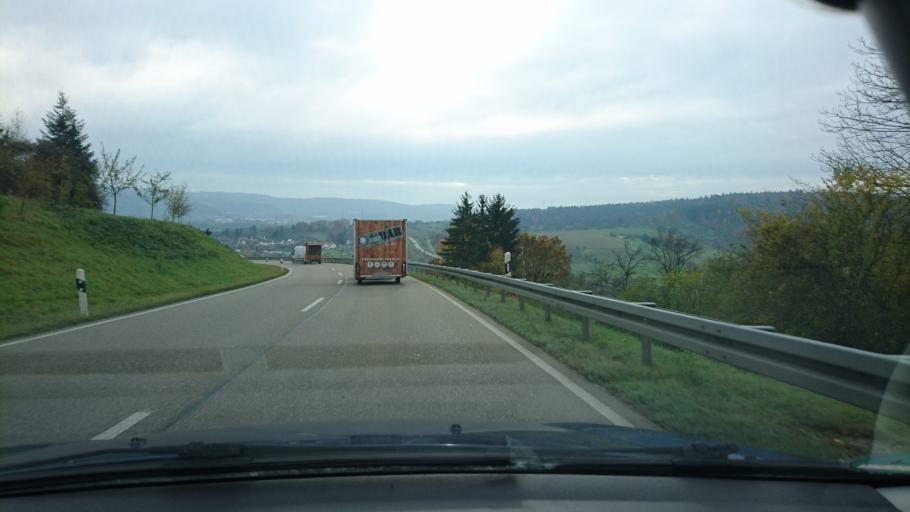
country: DE
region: Baden-Wuerttemberg
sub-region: Regierungsbezirk Stuttgart
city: Urbach
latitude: 48.8385
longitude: 9.5482
